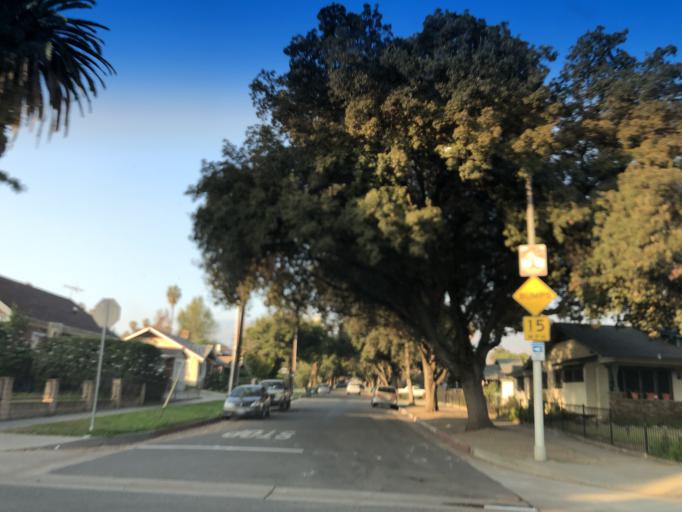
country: US
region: California
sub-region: Los Angeles County
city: Pasadena
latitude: 34.1543
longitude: -118.1244
